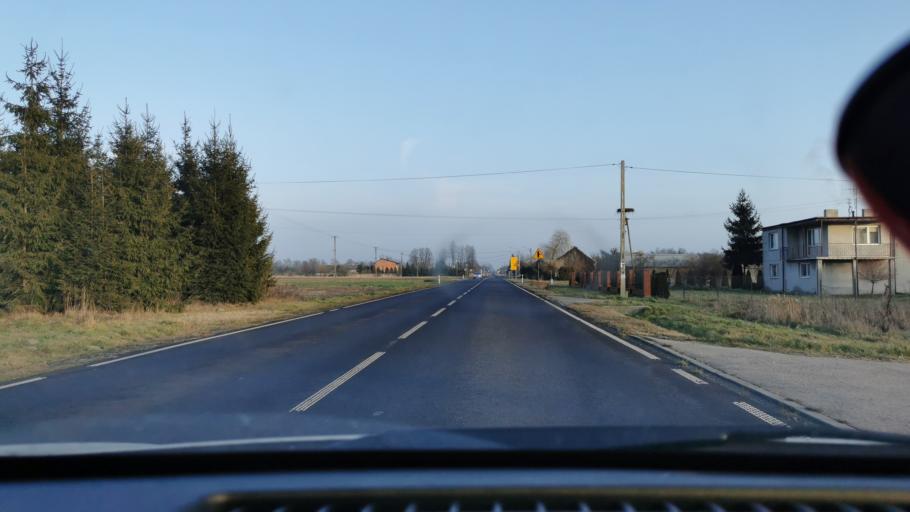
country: PL
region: Lodz Voivodeship
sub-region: Powiat belchatowski
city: Druzbice
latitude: 51.5107
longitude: 19.3681
